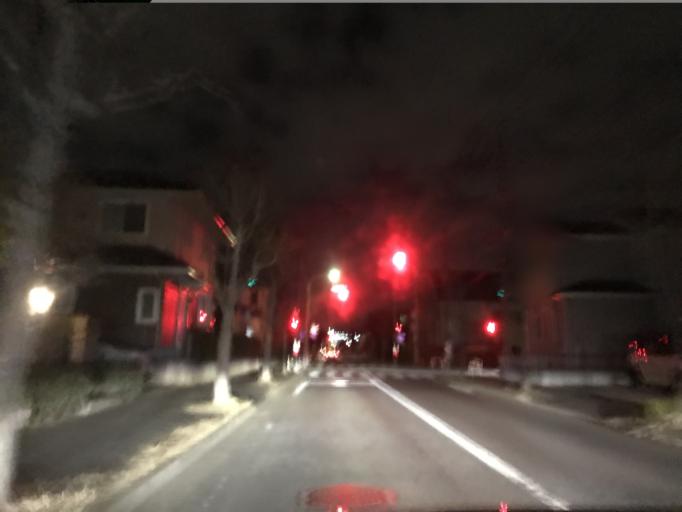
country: JP
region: Ibaraki
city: Naka
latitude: 36.0549
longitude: 140.1316
